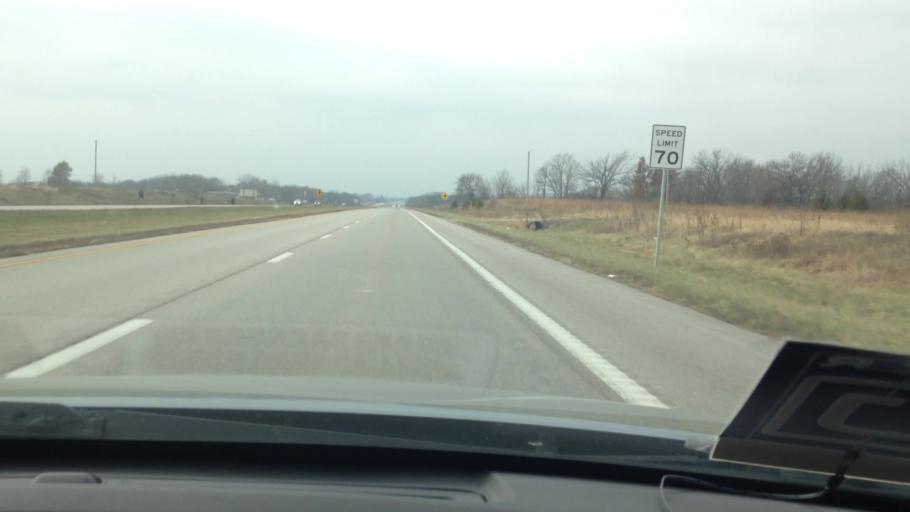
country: US
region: Missouri
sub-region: Cass County
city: Garden City
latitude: 38.5767
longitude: -94.2044
